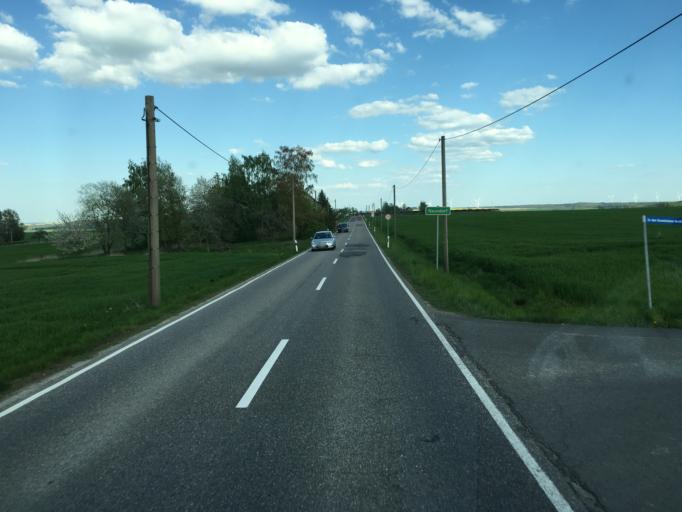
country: DE
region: Saxony
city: Niederstriegis
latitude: 51.0532
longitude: 13.1218
